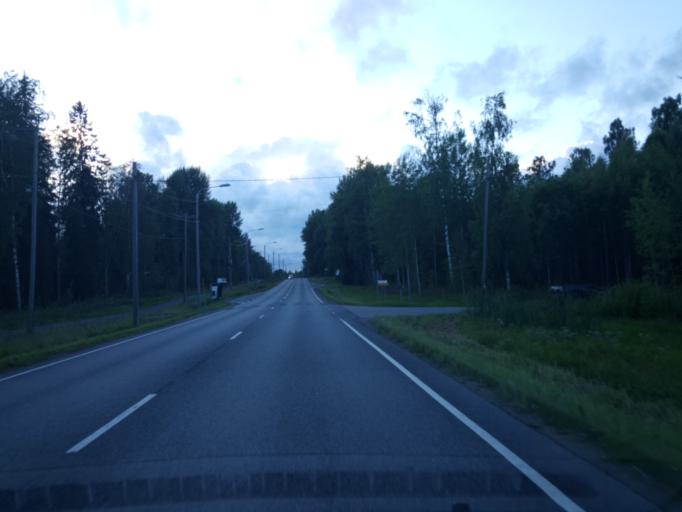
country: FI
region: Uusimaa
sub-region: Helsinki
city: Kilo
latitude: 60.3040
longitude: 24.7508
